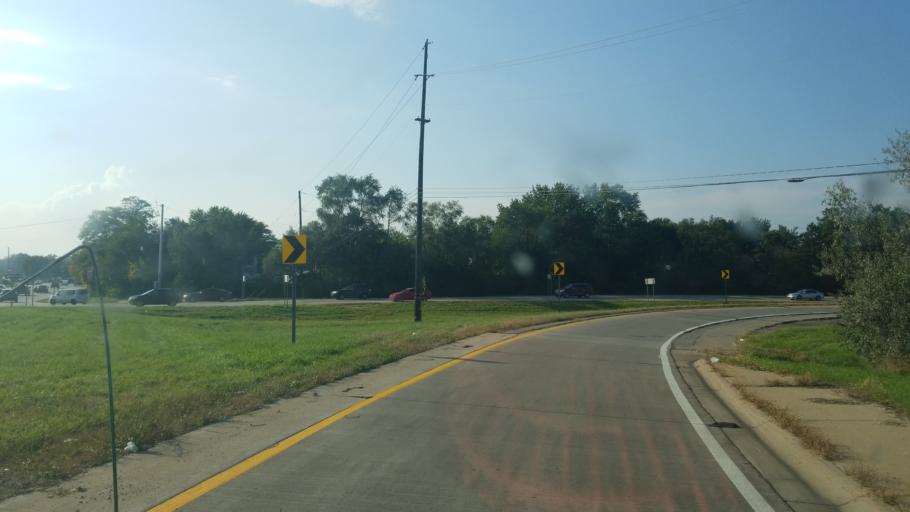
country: US
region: Michigan
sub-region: Wayne County
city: Plymouth
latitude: 42.3597
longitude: -83.4377
